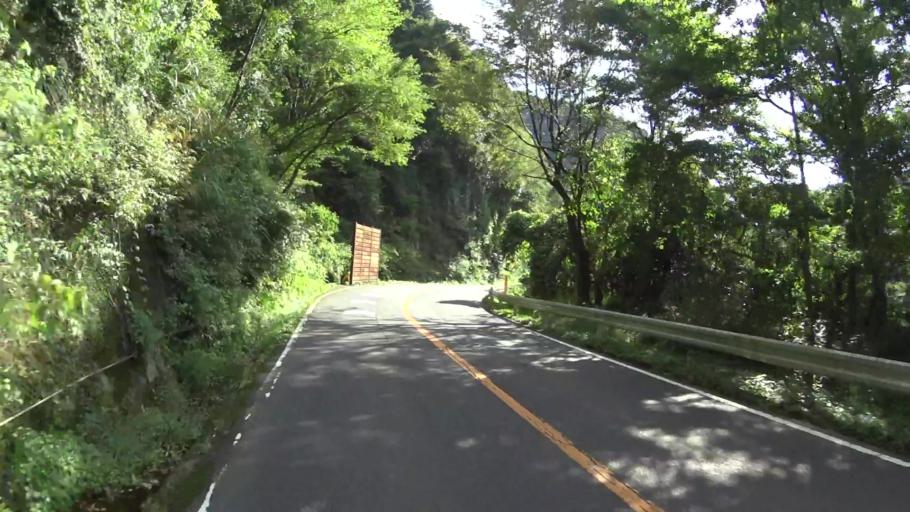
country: JP
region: Kyoto
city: Uji
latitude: 34.8931
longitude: 135.8687
